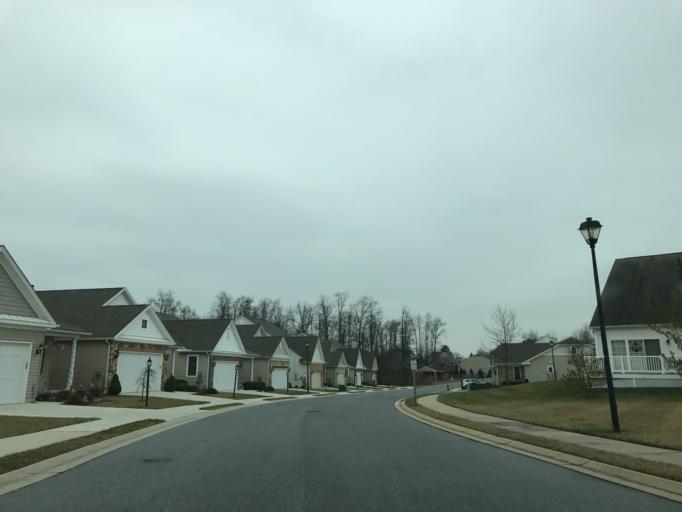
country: US
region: Maryland
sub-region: Carroll County
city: Taneytown
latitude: 39.6412
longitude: -77.1551
